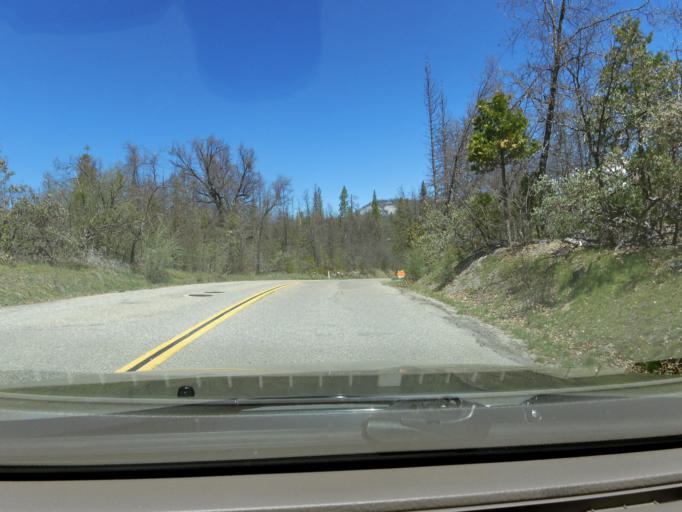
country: US
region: California
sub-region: Madera County
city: Oakhurst
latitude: 37.3295
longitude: -119.5832
